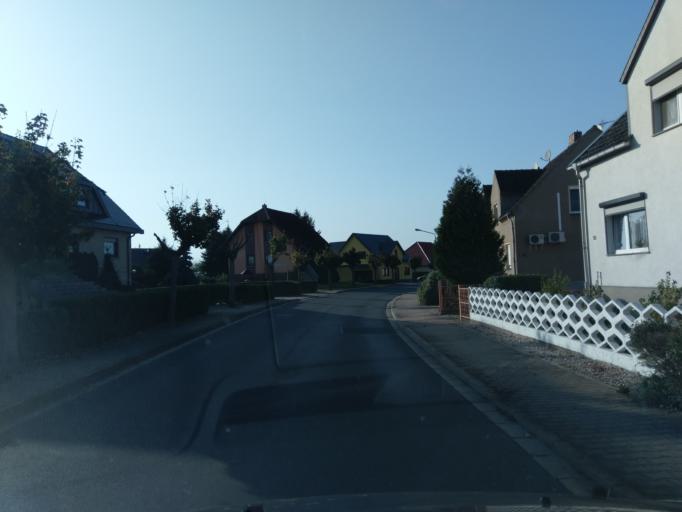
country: DE
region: Brandenburg
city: Falkenberg
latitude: 51.5731
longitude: 13.2482
